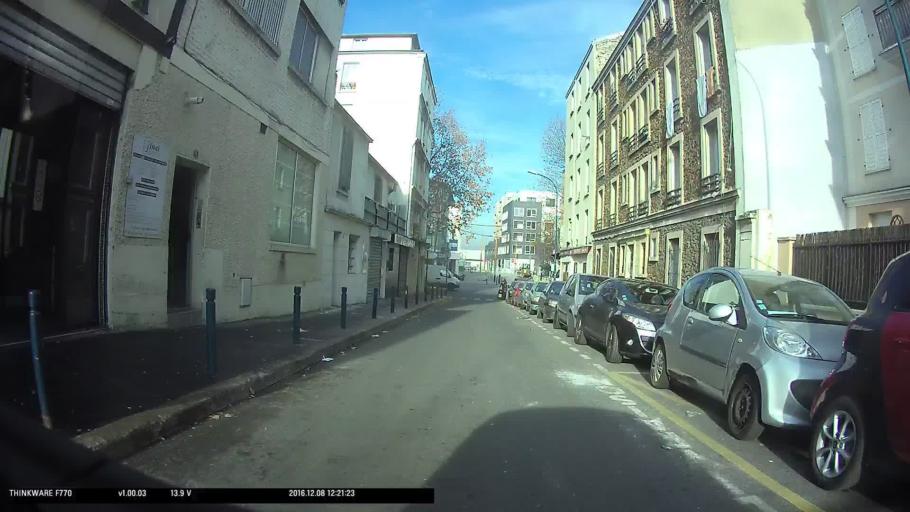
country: FR
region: Ile-de-France
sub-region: Departement de Seine-Saint-Denis
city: Pantin
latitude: 48.8937
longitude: 2.4189
